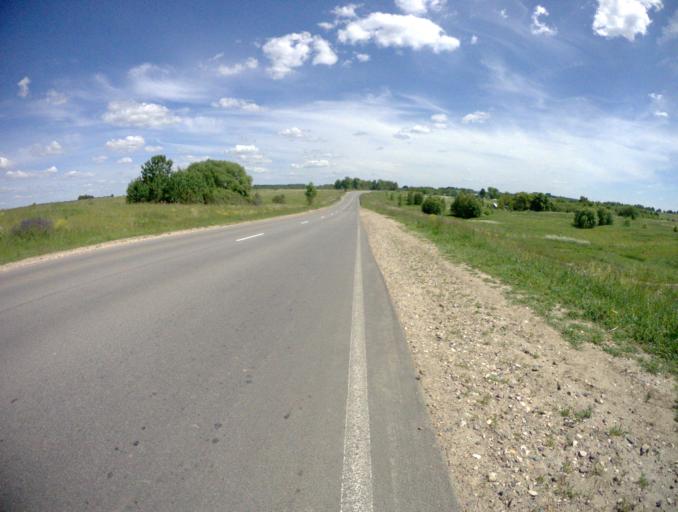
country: RU
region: Ivanovo
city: Gavrilov Posad
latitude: 56.3608
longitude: 40.0796
